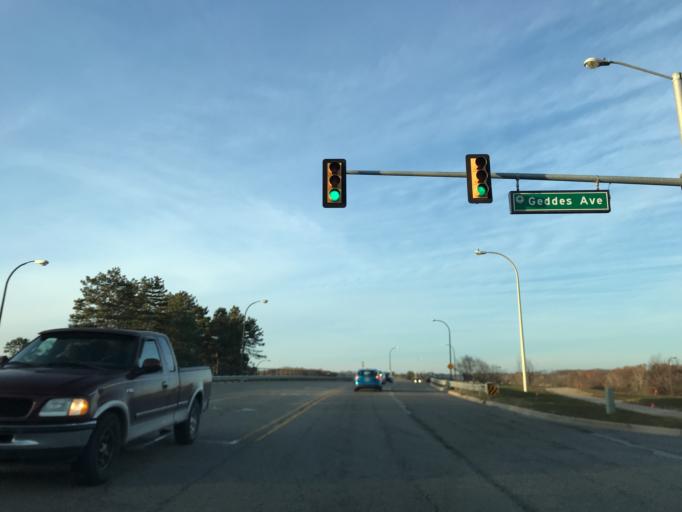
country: US
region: Michigan
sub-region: Washtenaw County
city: Ann Arbor
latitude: 42.2726
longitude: -83.6982
